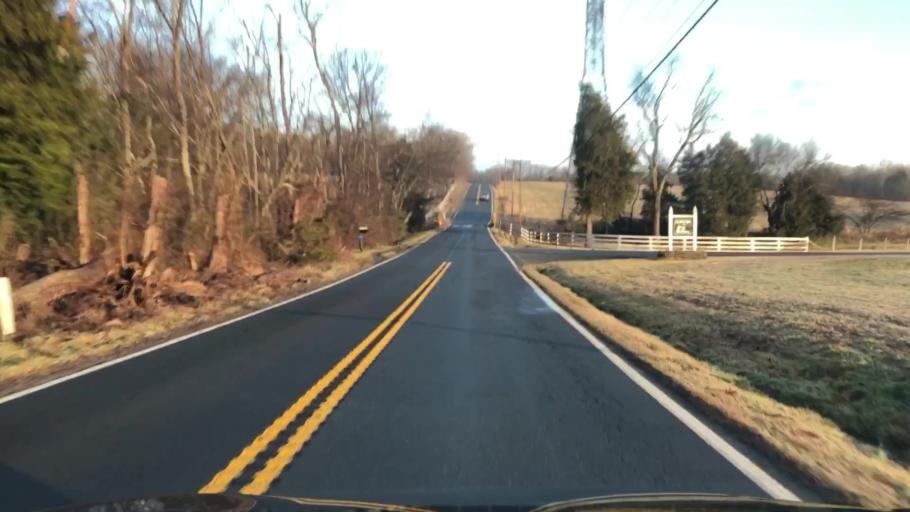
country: US
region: Virginia
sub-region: Fauquier County
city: Bealeton
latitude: 38.5633
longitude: -77.6748
